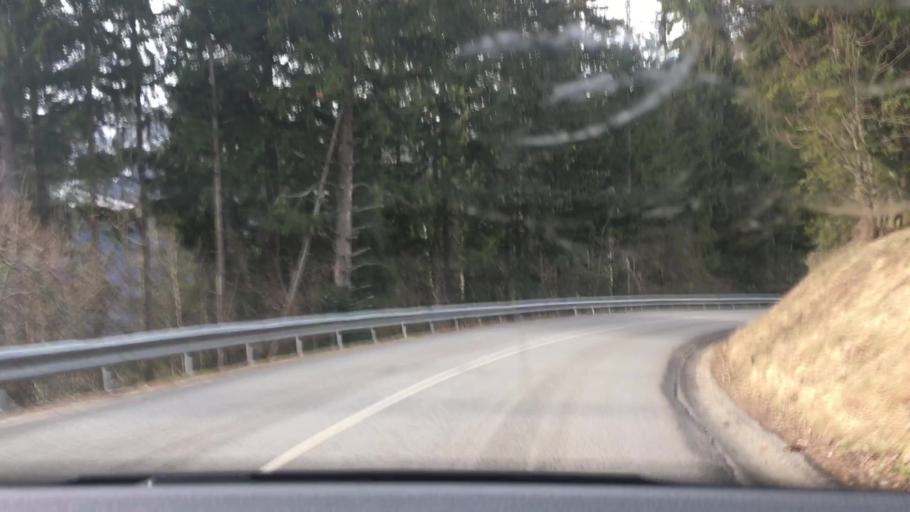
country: FR
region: Rhone-Alpes
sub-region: Departement de la Haute-Savoie
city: Abondance
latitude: 46.2833
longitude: 6.6427
